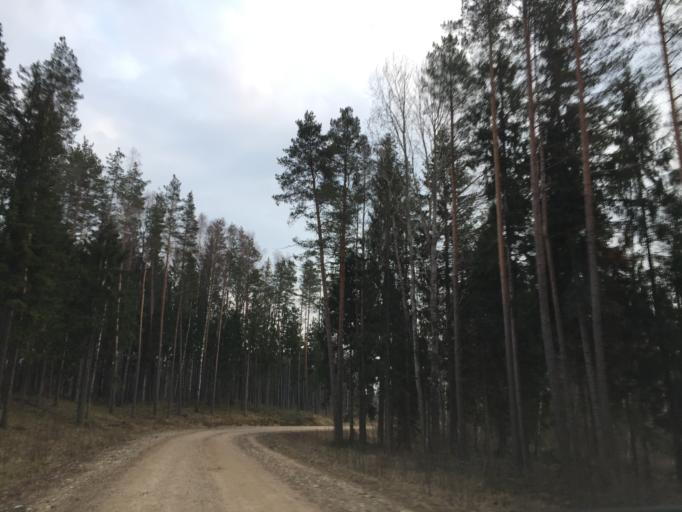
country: LV
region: Raunas
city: Rauna
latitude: 57.1352
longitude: 25.6034
